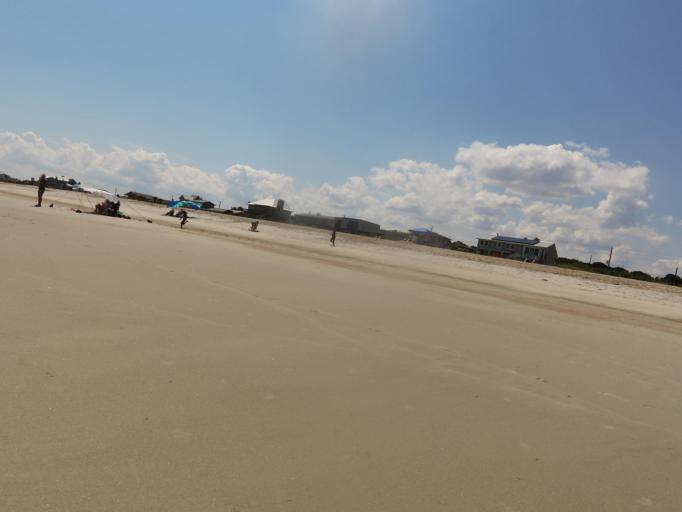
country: US
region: Florida
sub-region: Nassau County
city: Fernandina Beach
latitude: 30.6480
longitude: -81.4332
